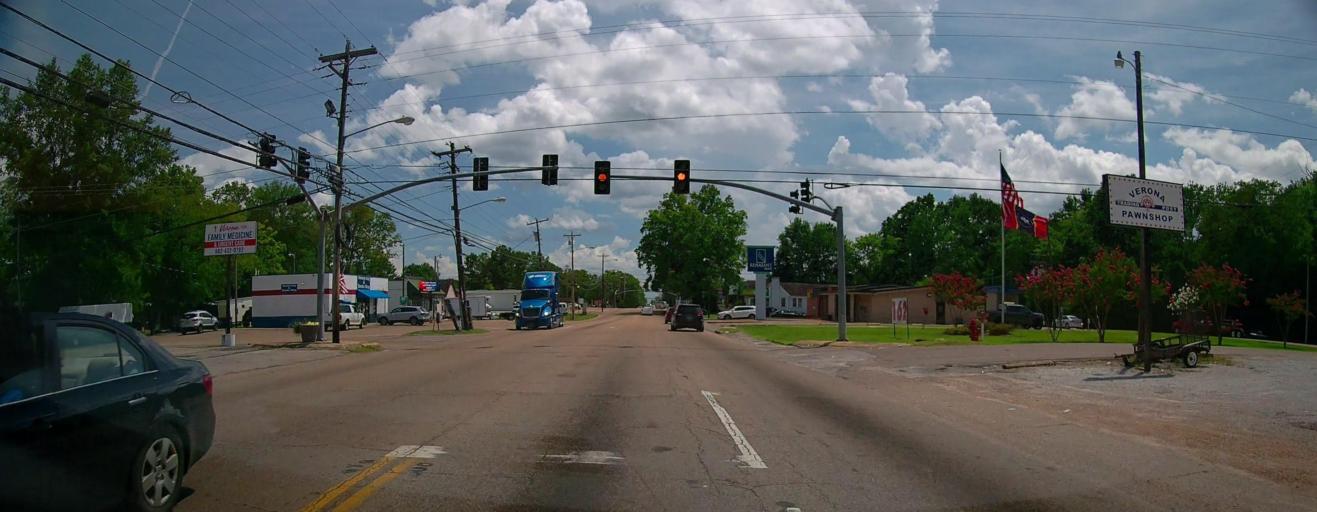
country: US
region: Mississippi
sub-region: Lee County
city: Verona
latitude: 34.1944
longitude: -88.7200
